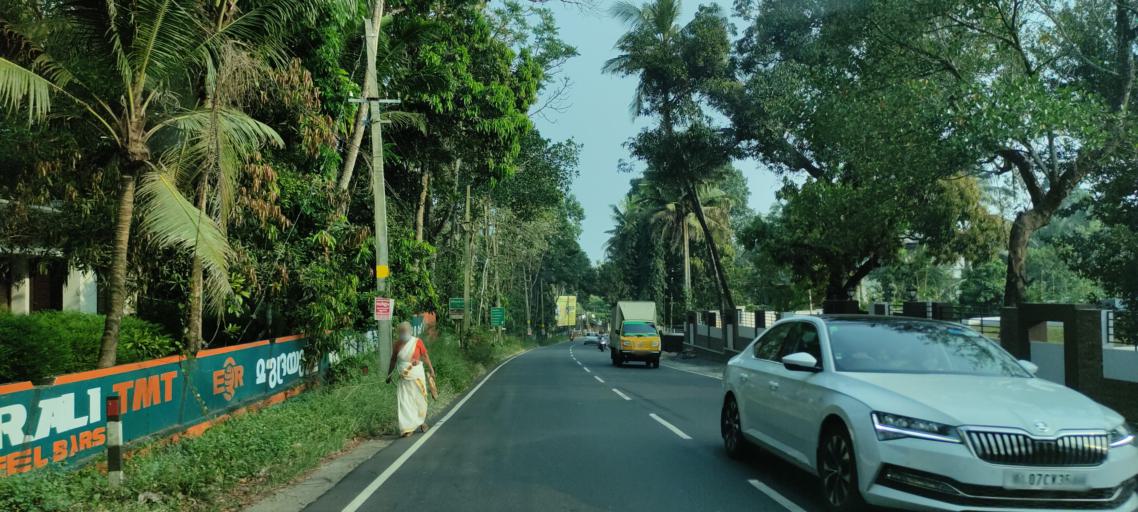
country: IN
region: Kerala
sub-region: Kottayam
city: Vaikam
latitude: 9.7585
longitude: 76.4952
